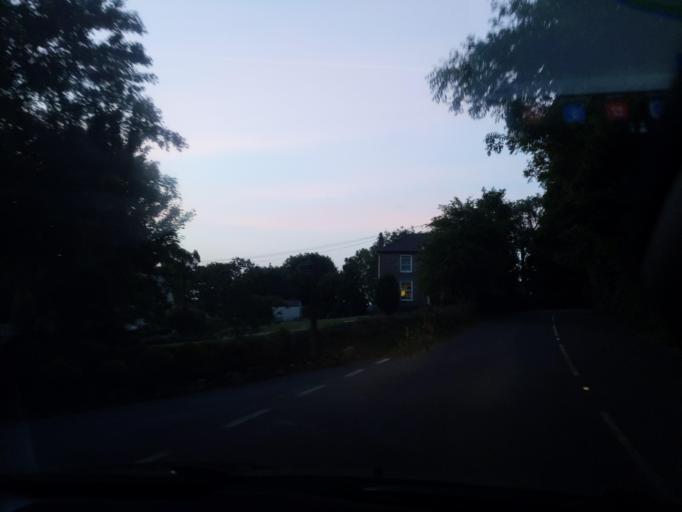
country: GB
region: England
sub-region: Cornwall
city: Camborne
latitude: 50.1948
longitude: -5.3086
